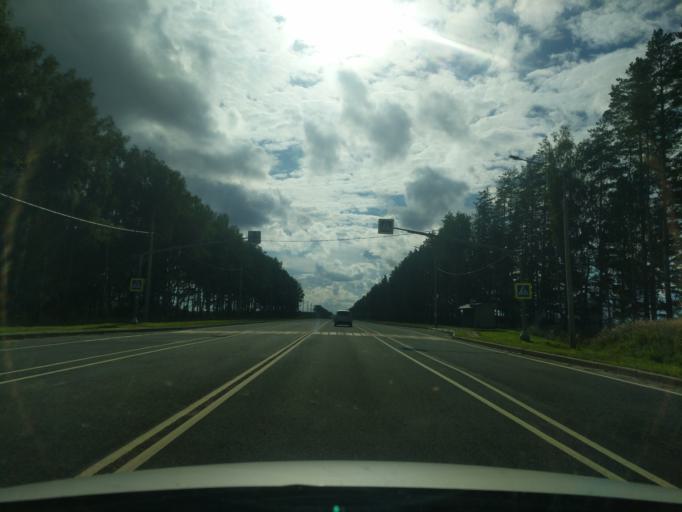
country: RU
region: Jaroslavl
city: Nekrasovskoye
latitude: 57.6183
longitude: 40.3520
